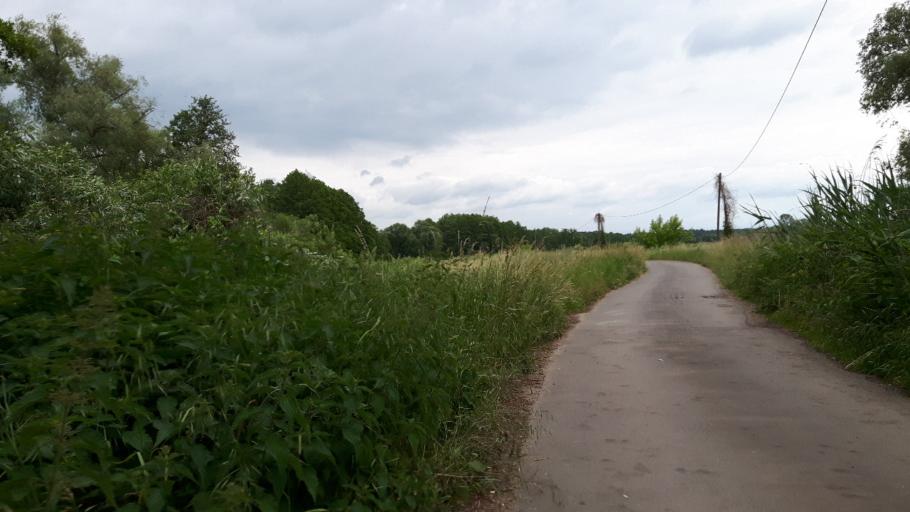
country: DE
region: Brandenburg
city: Oderberg
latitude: 52.8651
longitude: 14.0778
